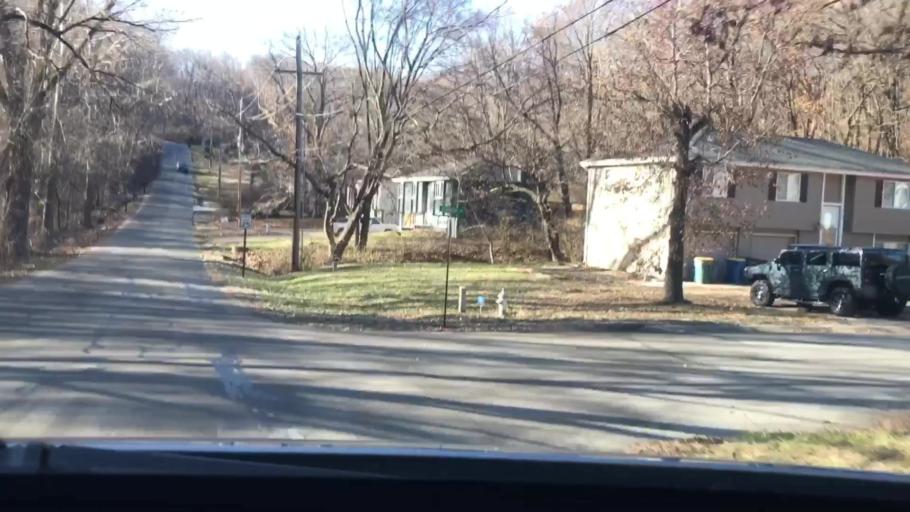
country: US
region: Missouri
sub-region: Platte County
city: Parkville
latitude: 39.1977
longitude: -94.6844
